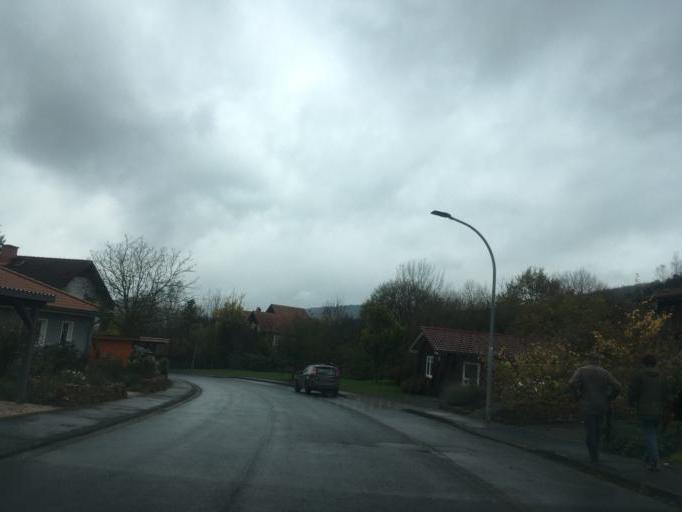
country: DE
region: Lower Saxony
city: Bodenfelde
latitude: 51.6416
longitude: 9.5676
